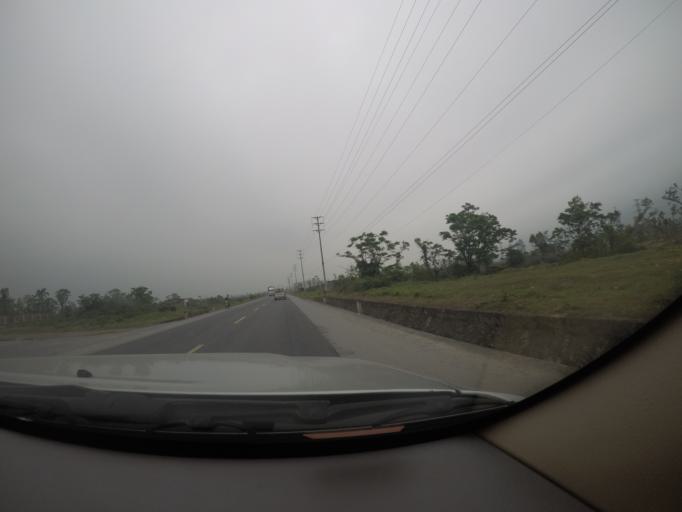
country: VN
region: Ha Tinh
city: Ky Anh
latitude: 18.0209
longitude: 106.3781
